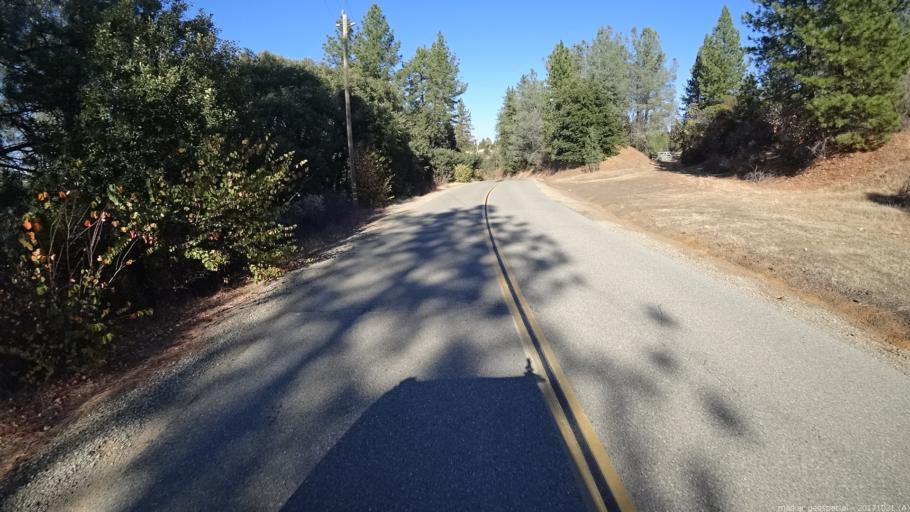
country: US
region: California
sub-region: Shasta County
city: Shingletown
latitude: 40.4659
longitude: -122.0041
